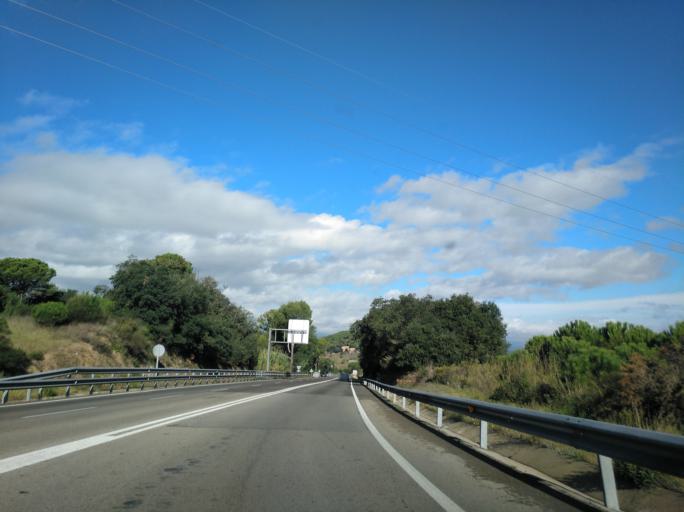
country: ES
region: Catalonia
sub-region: Provincia de Barcelona
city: Tordera
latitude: 41.6762
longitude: 2.7256
